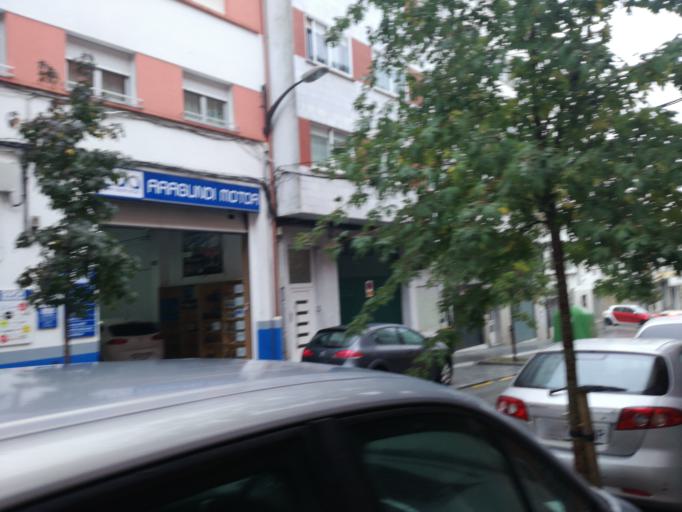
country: ES
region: Galicia
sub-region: Provincia da Coruna
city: Santiago de Compostela
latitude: 42.8776
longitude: -8.5356
